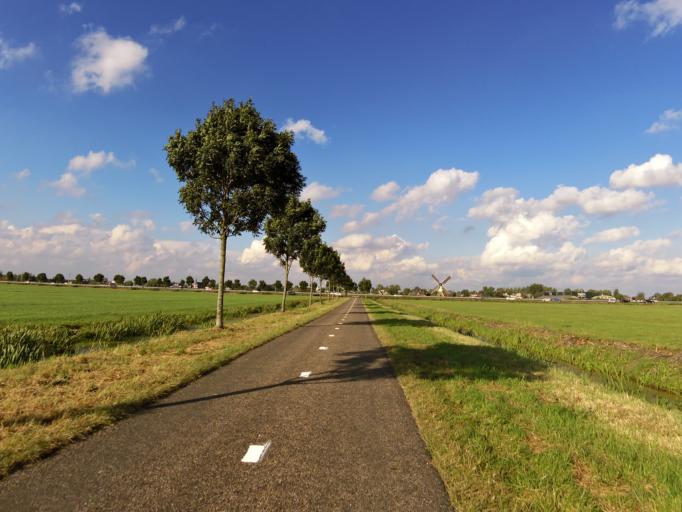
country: NL
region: South Holland
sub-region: Gemeente Rijnwoude
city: Benthuizen
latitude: 52.1222
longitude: 4.5628
